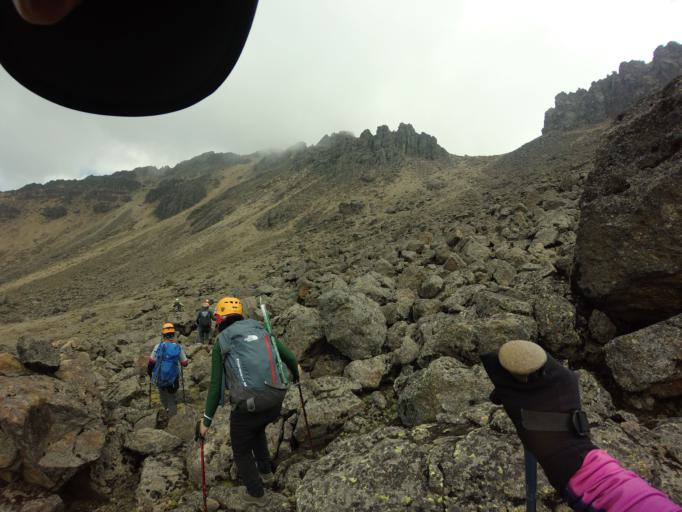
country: MX
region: Mexico
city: Amecameca de Juarez
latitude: 19.1485
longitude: -98.6380
